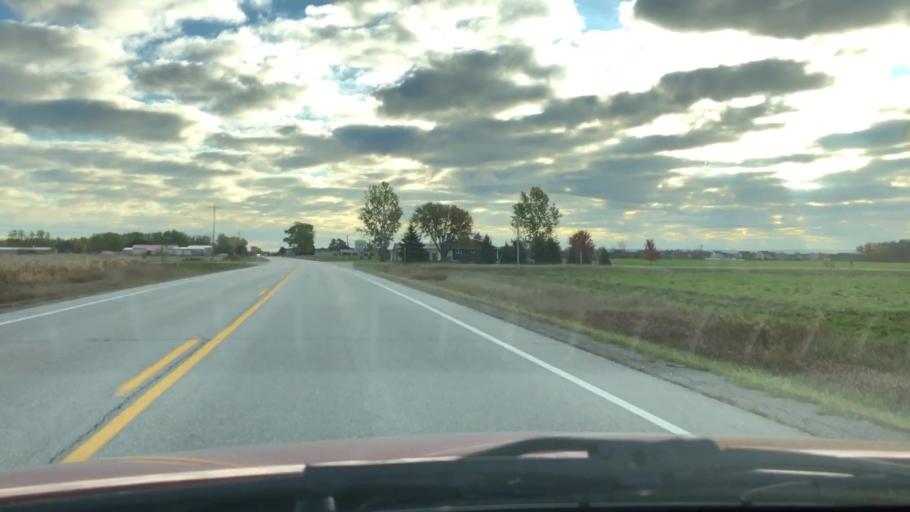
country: US
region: Wisconsin
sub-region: Brown County
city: Oneida
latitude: 44.4443
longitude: -88.1518
